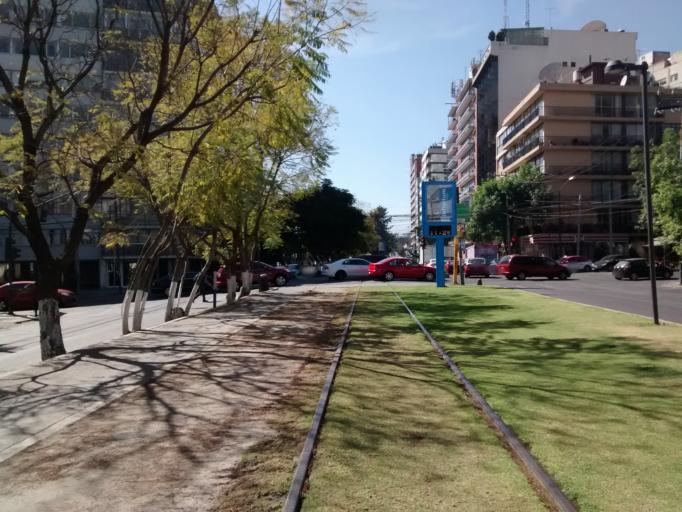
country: MX
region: Mexico City
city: Miguel Hidalgo
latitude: 19.4367
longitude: -99.2067
